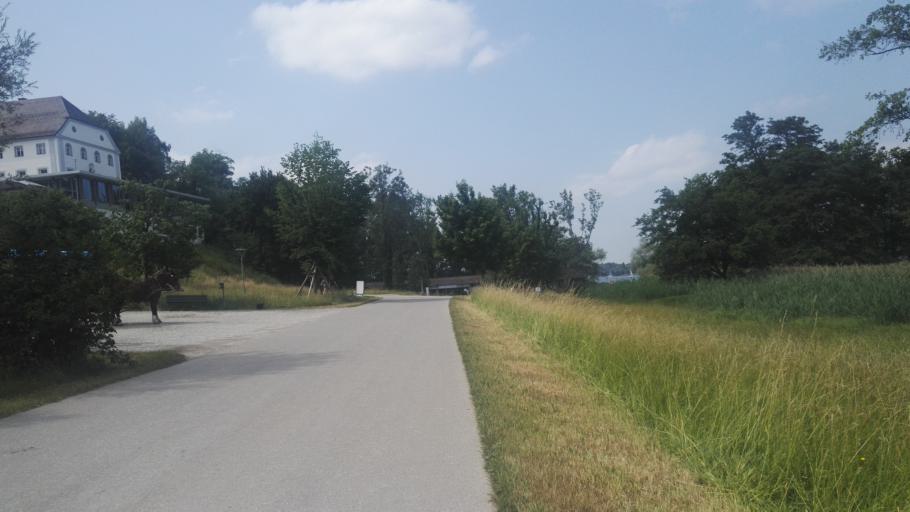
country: DE
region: Bavaria
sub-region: Upper Bavaria
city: Chiemsee
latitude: 47.8674
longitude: 12.3985
